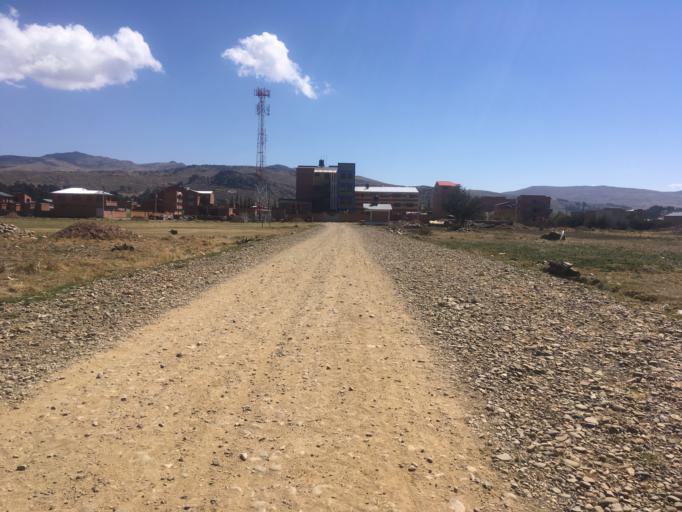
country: BO
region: La Paz
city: Huatajata
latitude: -16.1946
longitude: -68.7451
